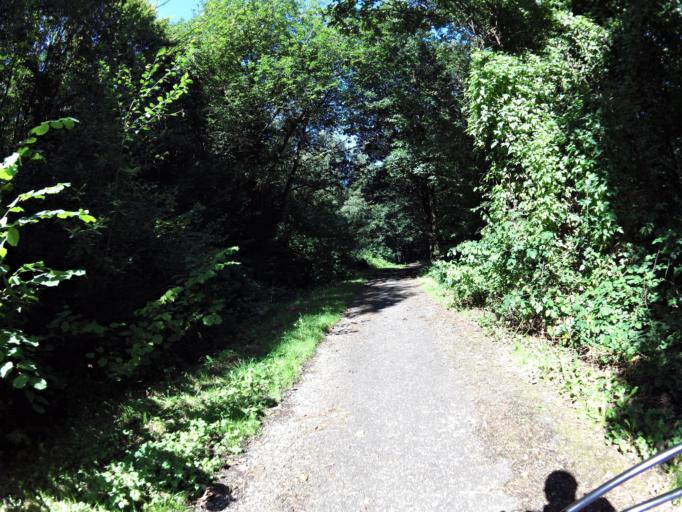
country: NL
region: Limburg
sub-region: Gemeente Kerkrade
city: Kerkrade
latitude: 50.8762
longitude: 6.0781
